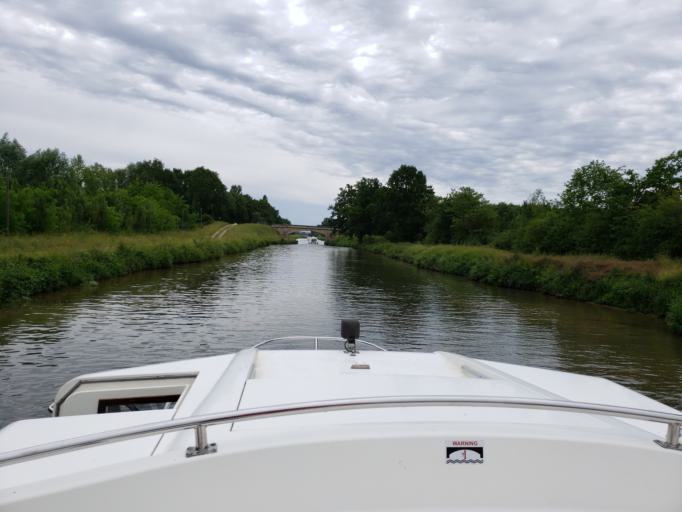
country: FR
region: Bourgogne
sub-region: Departement de l'Yonne
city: Appoigny
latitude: 47.8884
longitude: 3.5426
